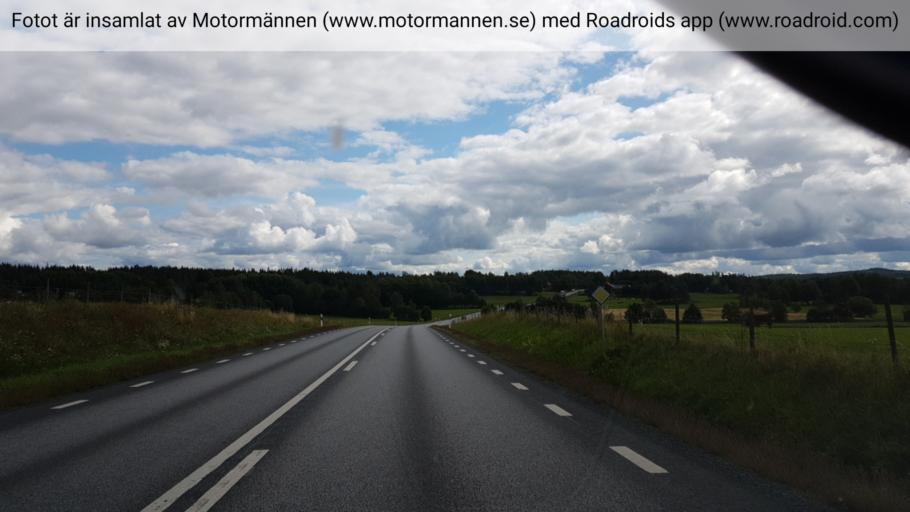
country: SE
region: Joenkoeping
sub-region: Jonkopings Kommun
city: Huskvarna
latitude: 57.7747
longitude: 14.3776
